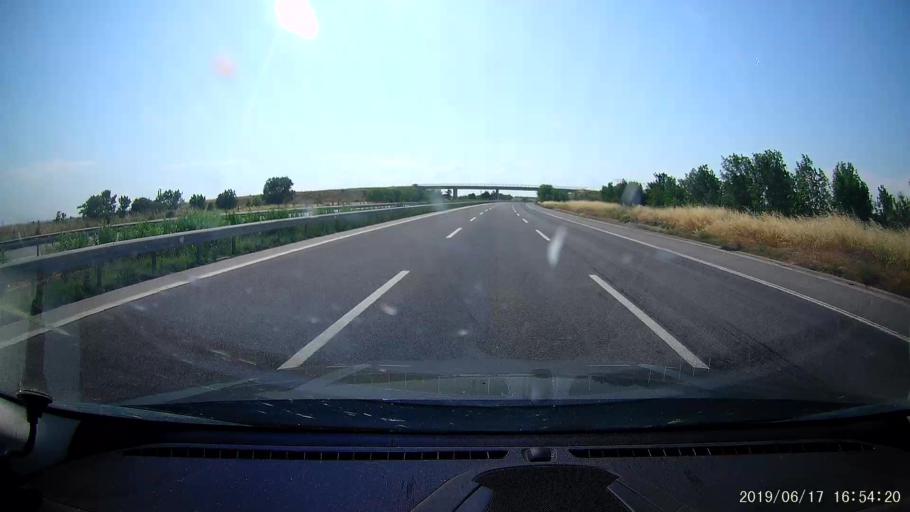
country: TR
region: Kirklareli
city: Inece
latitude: 41.5729
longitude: 26.9992
